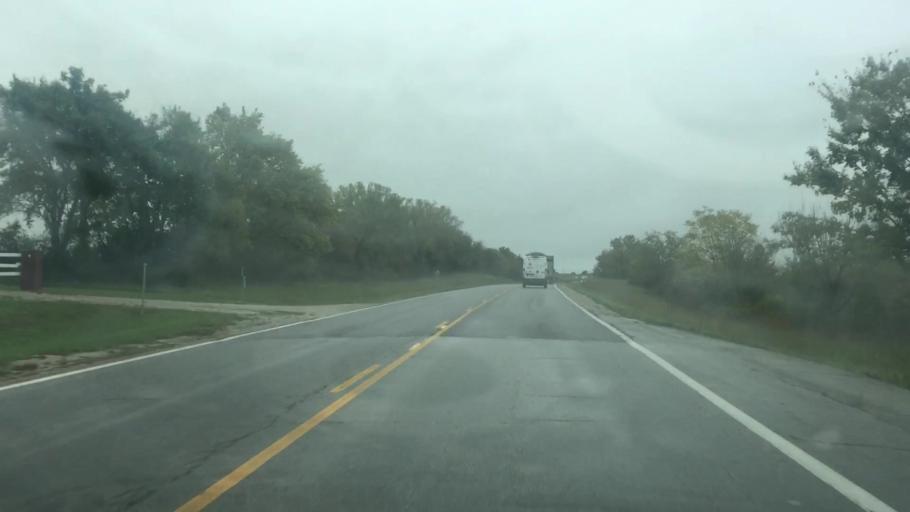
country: US
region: Kansas
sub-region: Anderson County
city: Garnett
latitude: 38.2031
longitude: -95.2493
